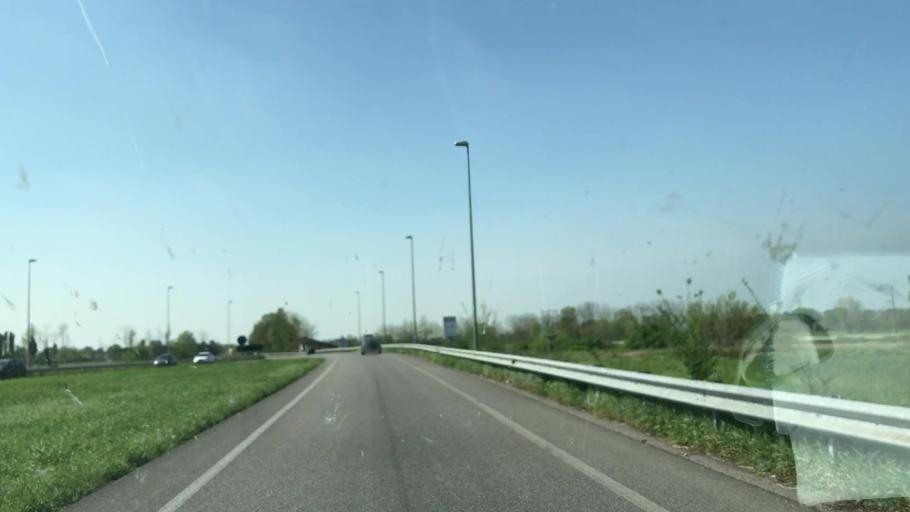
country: IT
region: Lombardy
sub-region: Provincia di Mantova
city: Marmirolo
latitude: 45.2207
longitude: 10.7425
